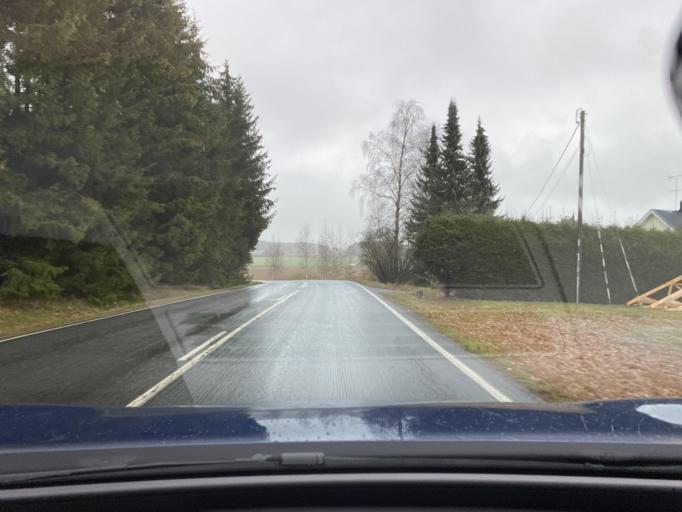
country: FI
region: Varsinais-Suomi
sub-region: Loimaa
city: Alastaro
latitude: 60.9371
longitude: 22.8692
